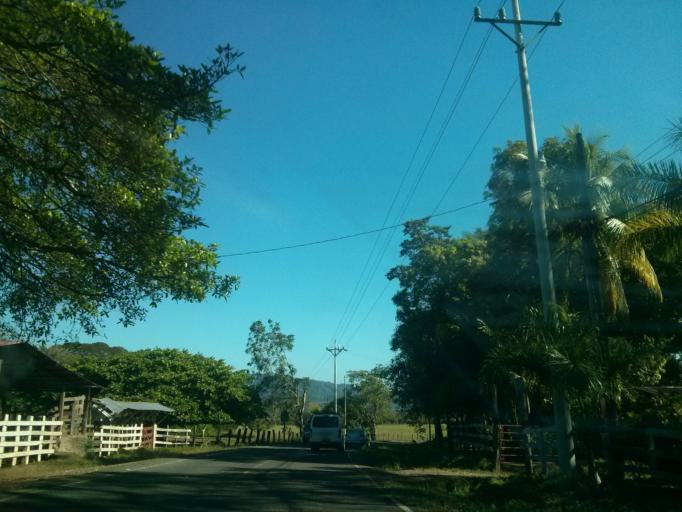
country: CR
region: Puntarenas
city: Paquera
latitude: 9.7019
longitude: -85.0539
